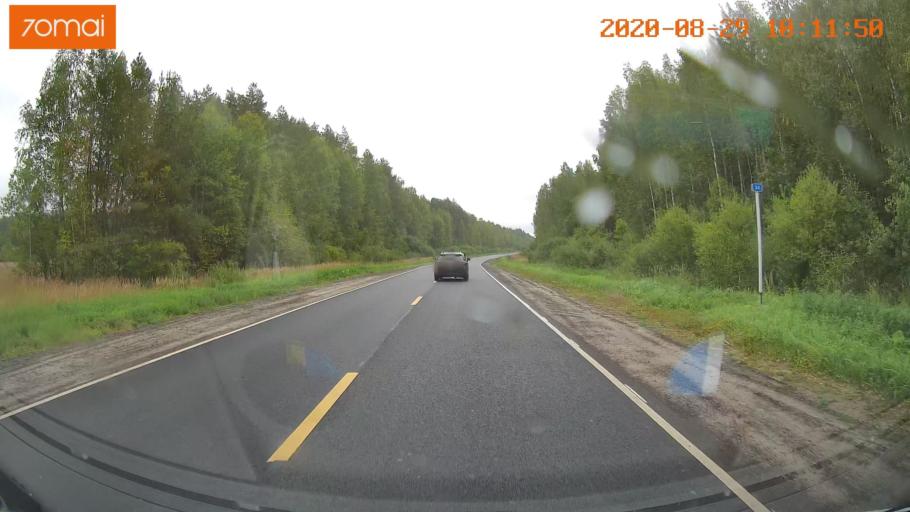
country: RU
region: Ivanovo
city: Kuznechikha
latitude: 57.3744
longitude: 42.6940
